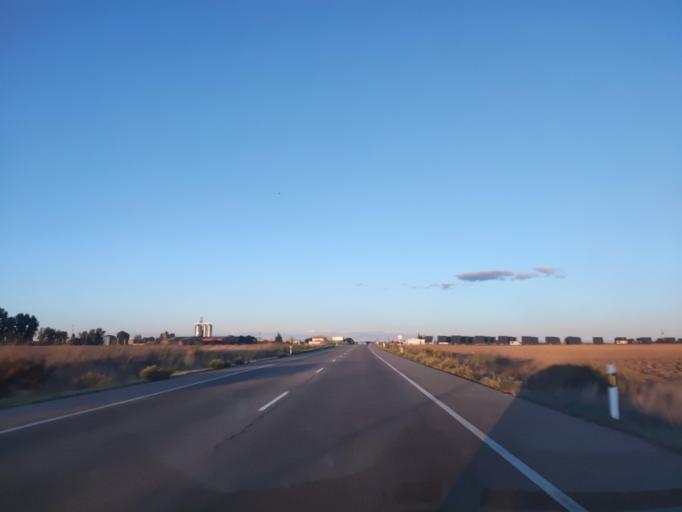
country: ES
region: Castille and Leon
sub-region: Provincia de Salamanca
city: La Fuente de San Esteban
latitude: 40.7873
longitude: -6.2553
